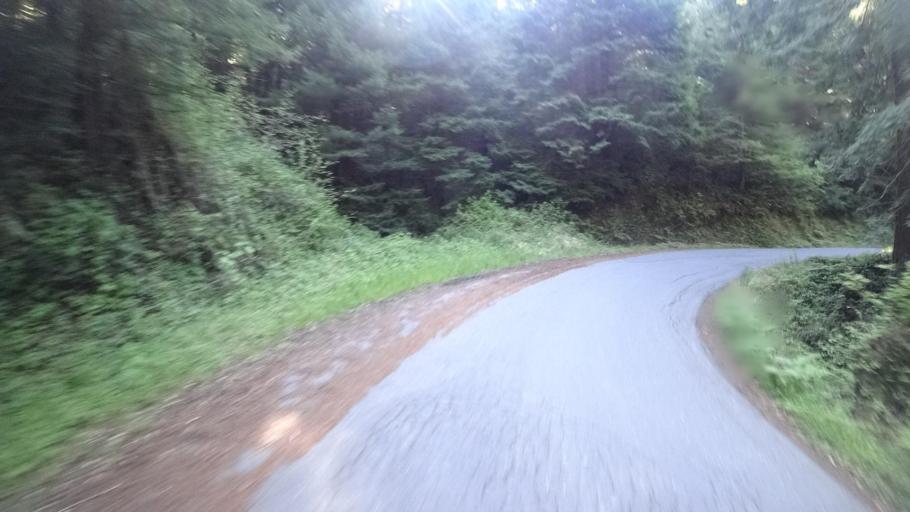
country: US
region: California
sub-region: Humboldt County
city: Rio Dell
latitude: 40.4578
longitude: -123.9937
